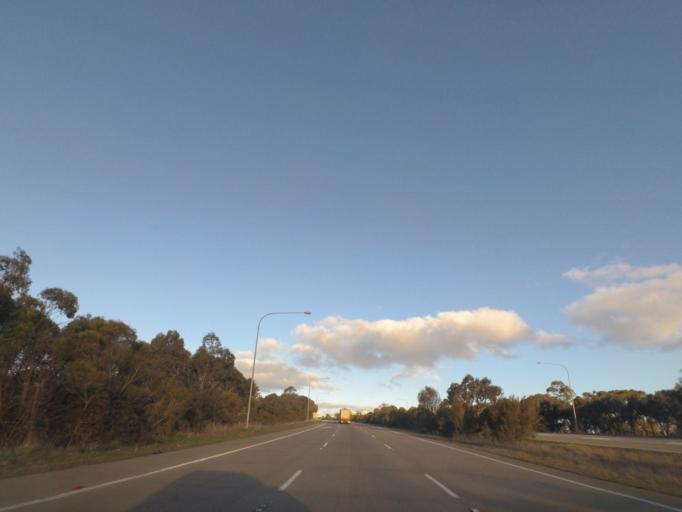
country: AU
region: New South Wales
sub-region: Yass Valley
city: Yass
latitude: -34.8031
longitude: 148.8787
